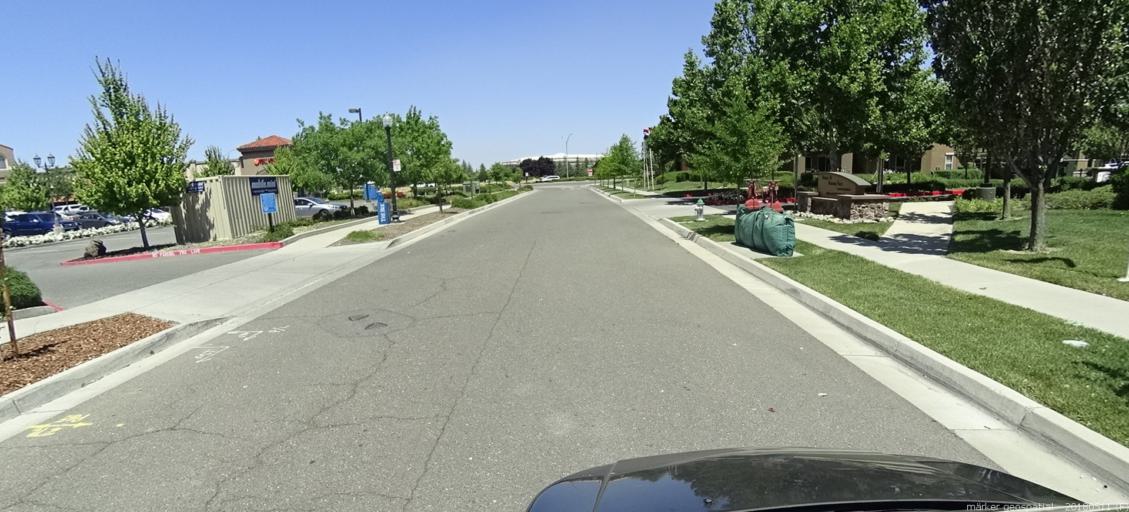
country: US
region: California
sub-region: Yolo County
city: West Sacramento
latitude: 38.6420
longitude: -121.5180
